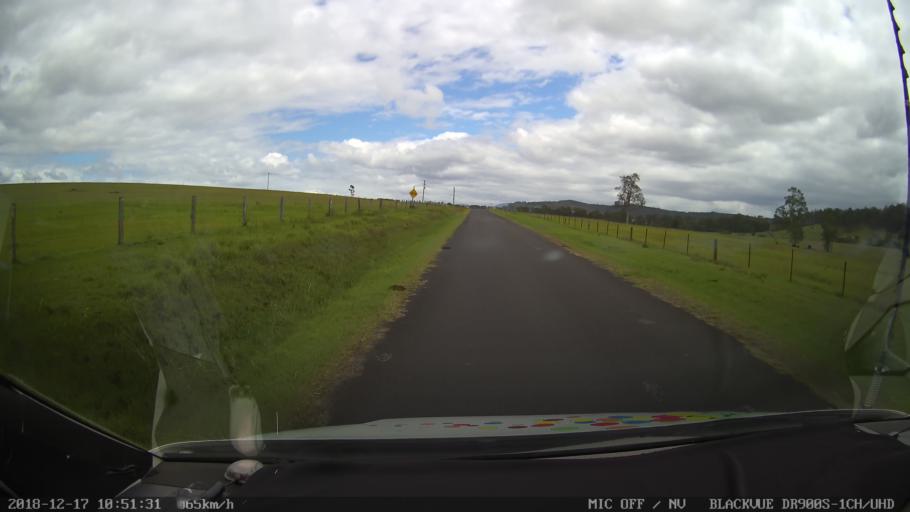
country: AU
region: New South Wales
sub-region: Tenterfield Municipality
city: Carrolls Creek
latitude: -28.8509
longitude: 152.5668
